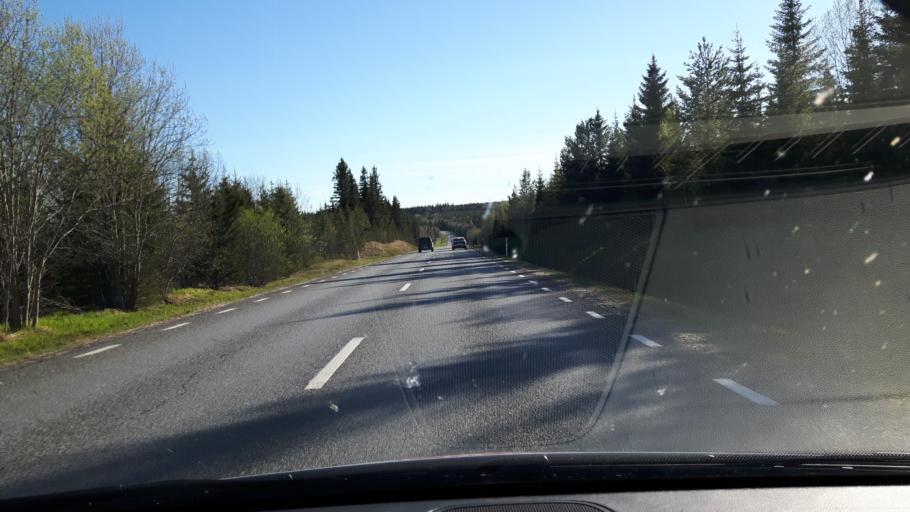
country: SE
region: Jaemtland
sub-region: OEstersunds Kommun
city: Lit
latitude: 63.4743
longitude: 15.2063
